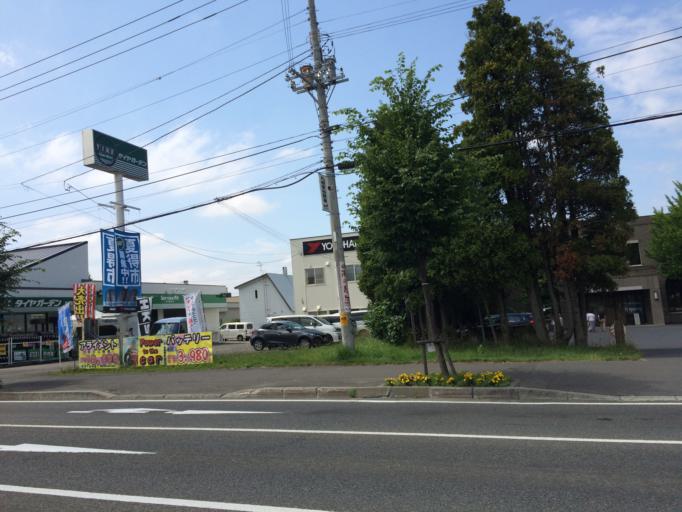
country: JP
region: Hokkaido
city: Ebetsu
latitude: 43.0513
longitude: 141.4841
